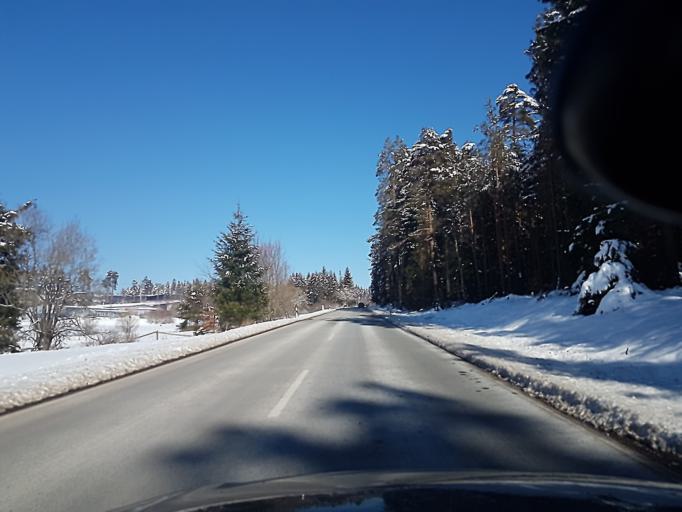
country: DE
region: Baden-Wuerttemberg
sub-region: Freiburg Region
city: Konigsfeld im Schwarzwald
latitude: 48.1249
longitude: 8.3943
